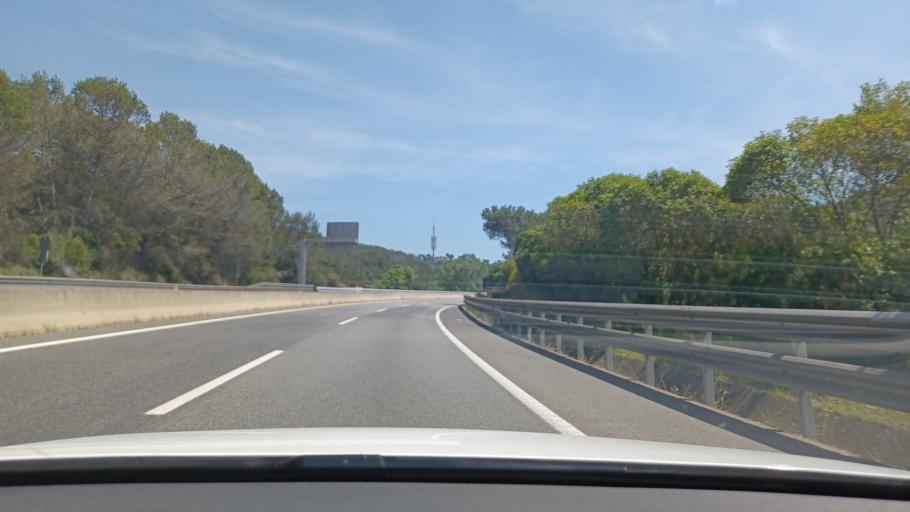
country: ES
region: Catalonia
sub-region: Provincia de Barcelona
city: Sant Cugat del Valles
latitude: 41.4324
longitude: 2.0802
